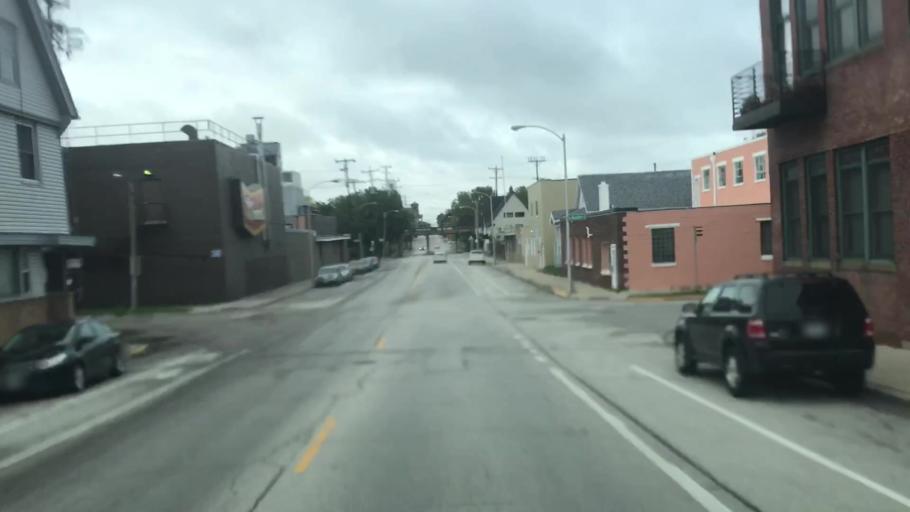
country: US
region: Wisconsin
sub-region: Milwaukee County
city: Milwaukee
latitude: 43.0029
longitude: -87.9065
